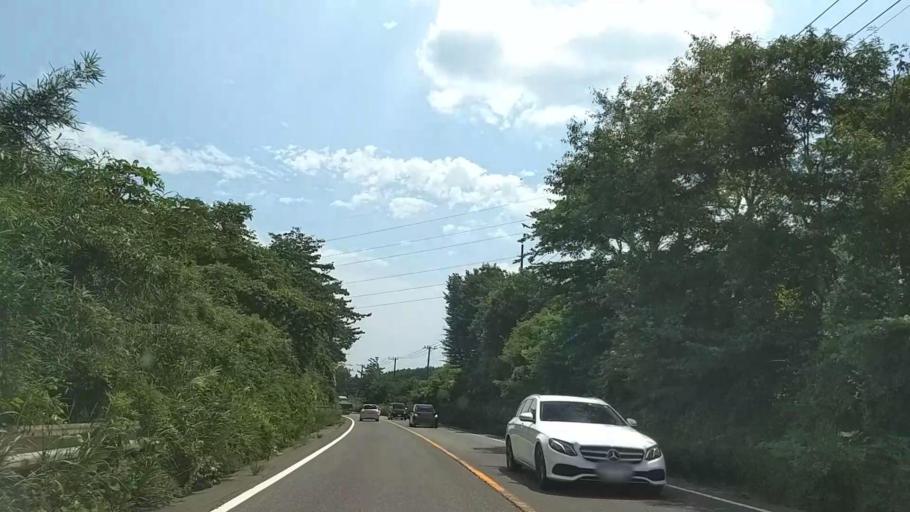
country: JP
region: Shizuoka
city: Fujinomiya
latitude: 35.3445
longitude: 138.5874
